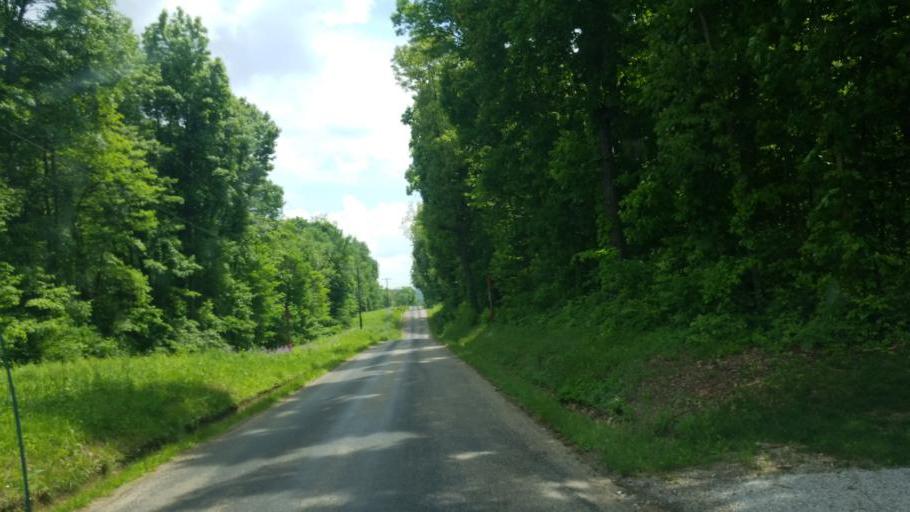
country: US
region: Ohio
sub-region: Ashland County
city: Ashland
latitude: 40.7819
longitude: -82.3397
